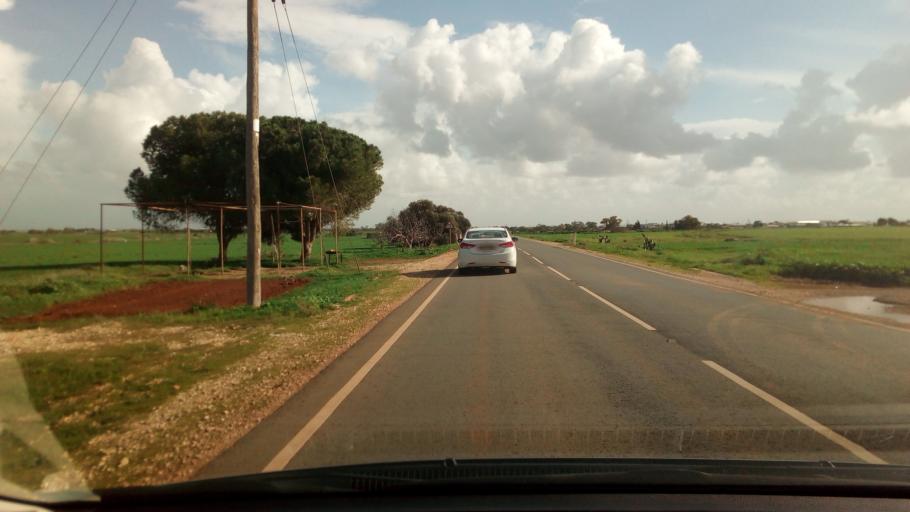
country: CY
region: Ammochostos
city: Achna
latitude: 35.0466
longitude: 33.7779
